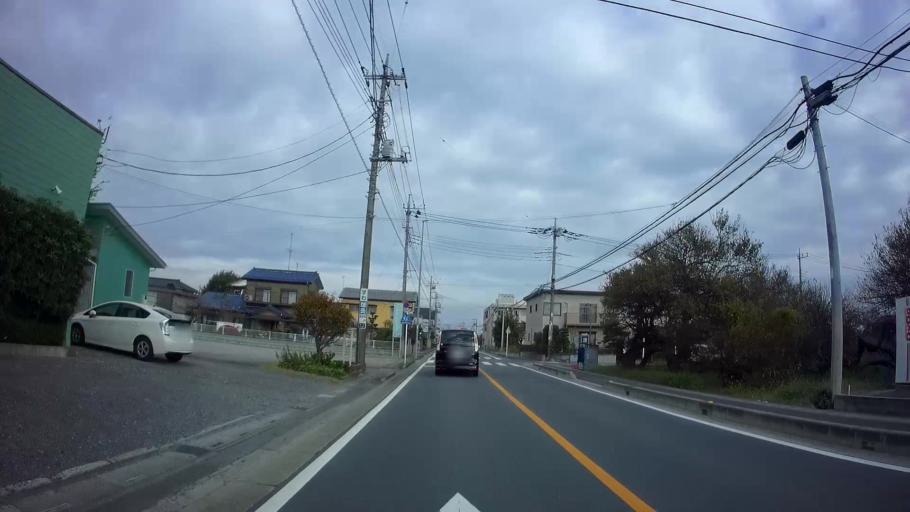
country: JP
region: Saitama
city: Okegawa
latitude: 36.0141
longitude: 139.5176
